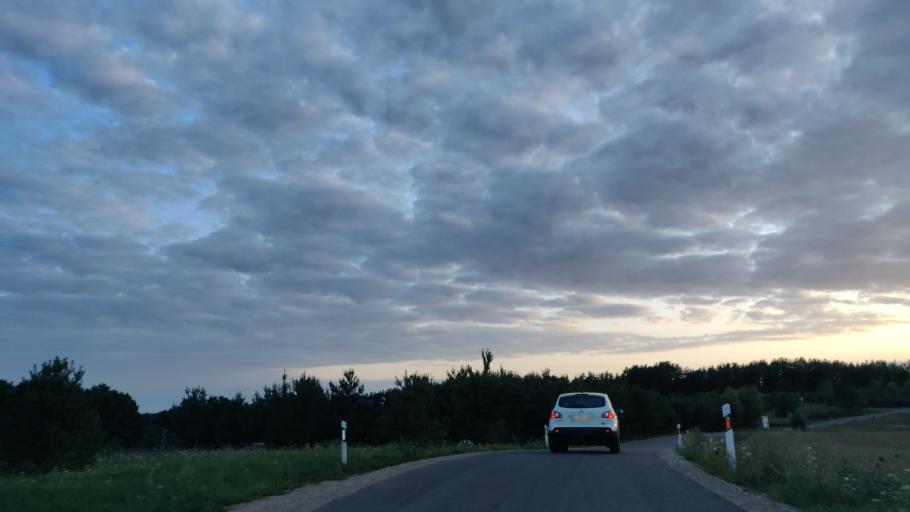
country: LT
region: Vilnius County
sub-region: Trakai
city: Rudiskes
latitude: 54.6049
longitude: 24.7895
